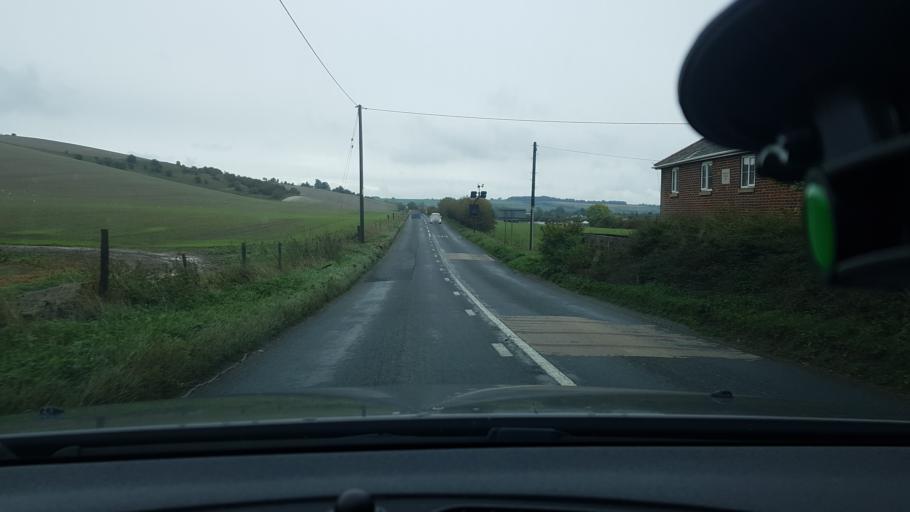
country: GB
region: England
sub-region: Borough of Swindon
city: Chiseldon
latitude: 51.4832
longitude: -1.7143
